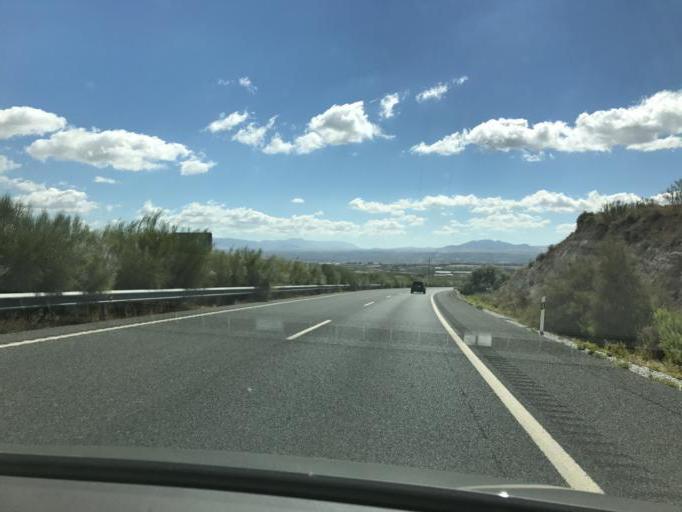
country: ES
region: Andalusia
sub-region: Provincia de Granada
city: Baza
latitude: 37.5152
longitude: -2.7963
